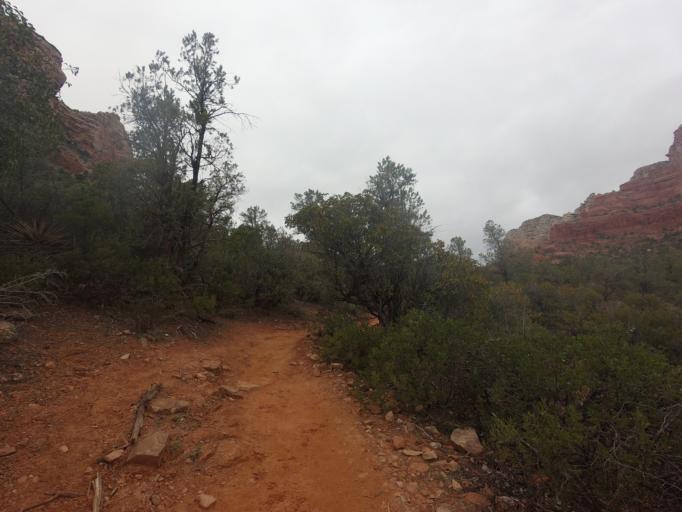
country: US
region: Arizona
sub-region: Yavapai County
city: Village of Oak Creek (Big Park)
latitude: 34.8027
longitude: -111.7475
